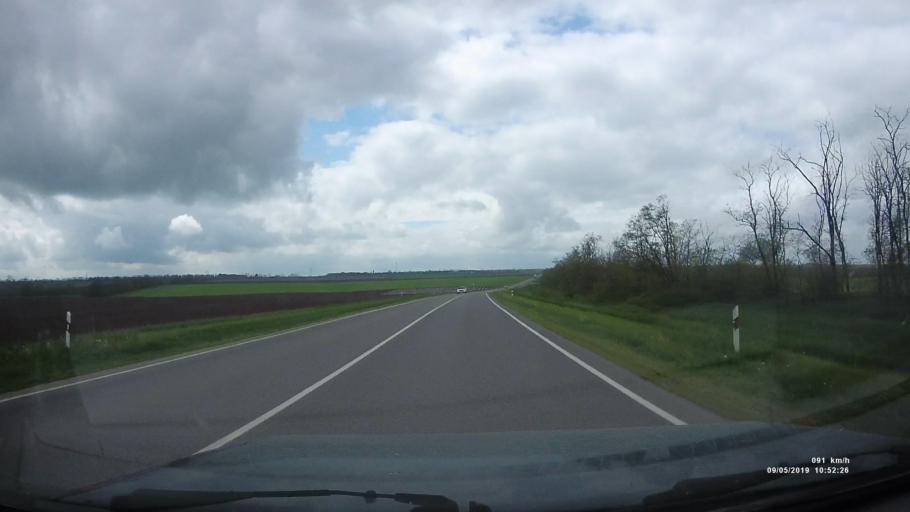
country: RU
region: Rostov
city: Peshkovo
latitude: 46.9008
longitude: 39.3530
